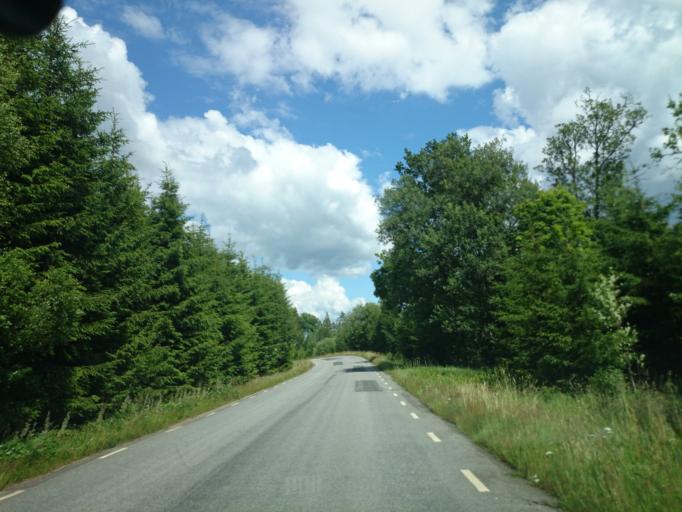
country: SE
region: Joenkoeping
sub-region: Varnamo Kommun
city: Forsheda
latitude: 57.0769
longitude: 13.8697
